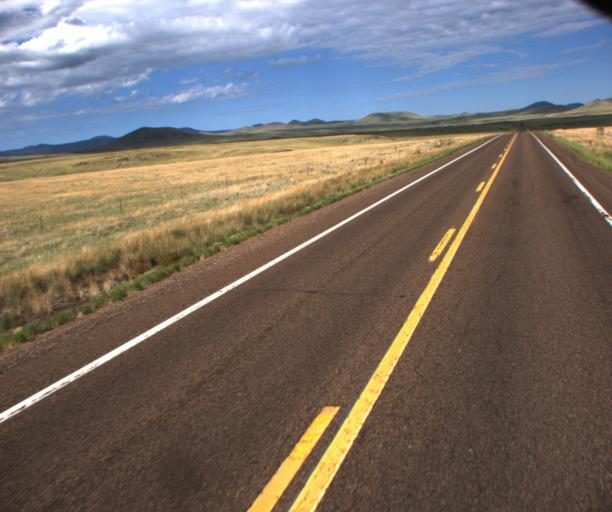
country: US
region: Arizona
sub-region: Apache County
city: Springerville
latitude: 34.1929
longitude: -109.3635
